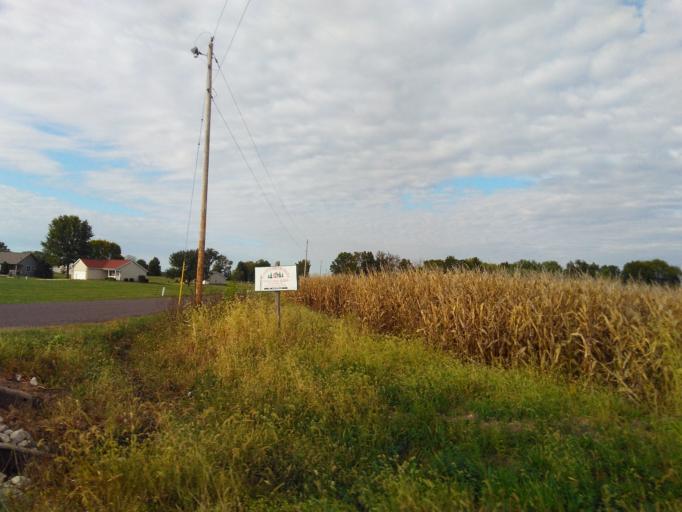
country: US
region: Illinois
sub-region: Bond County
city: Greenville
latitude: 38.9019
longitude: -89.3913
